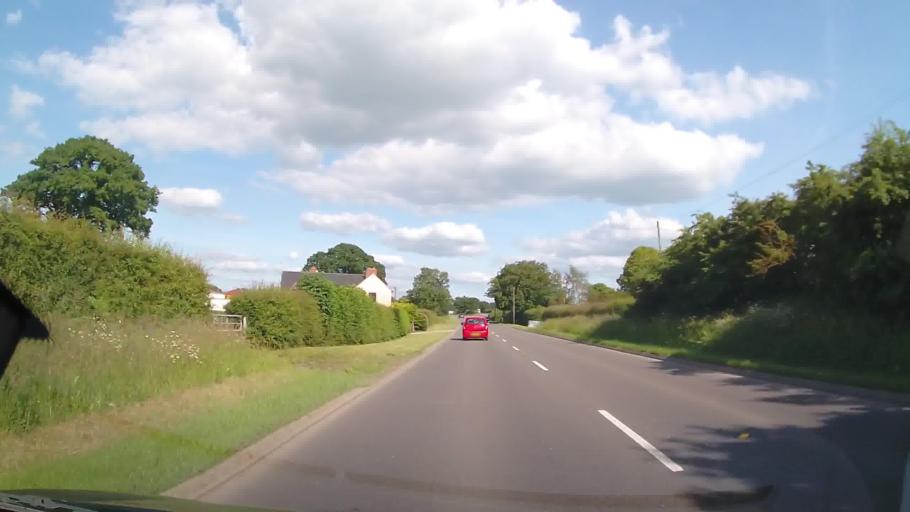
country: GB
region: England
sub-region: Shropshire
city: Westbury
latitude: 52.6995
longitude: -2.9888
